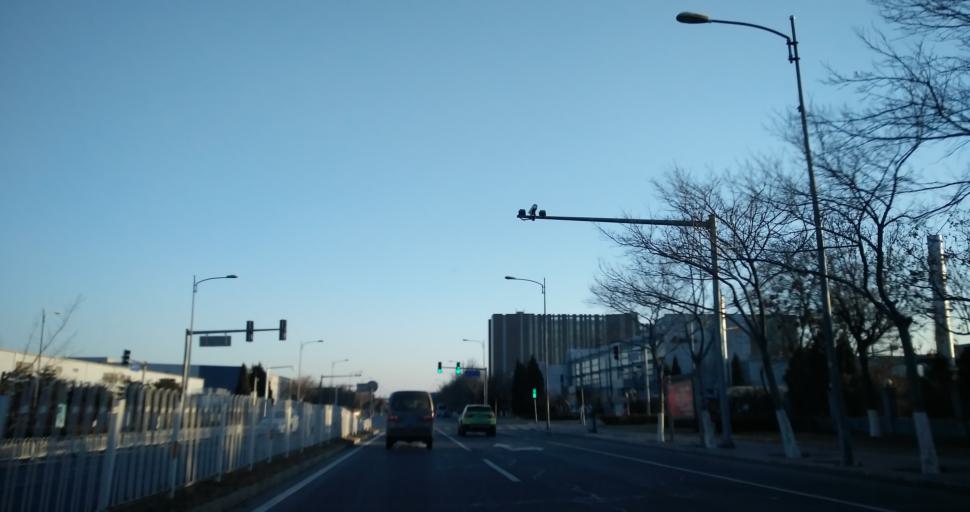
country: CN
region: Beijing
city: Jiugong
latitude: 39.7864
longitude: 116.5178
